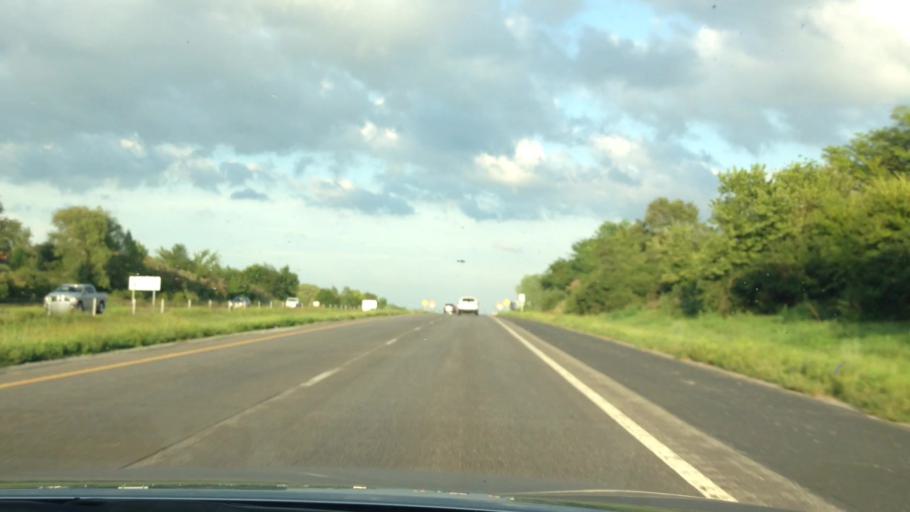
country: US
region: Missouri
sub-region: Clay County
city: Pleasant Valley
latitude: 39.2440
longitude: -94.4943
